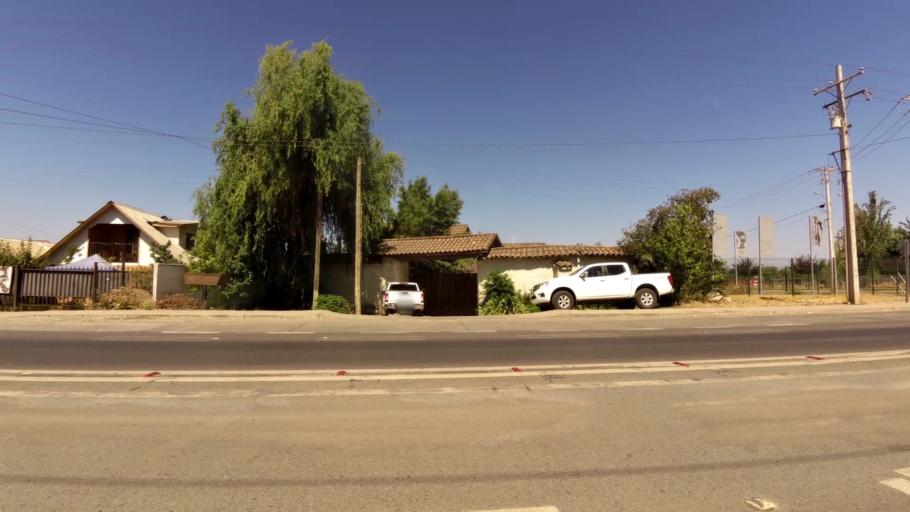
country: CL
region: Maule
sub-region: Provincia de Talca
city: Talca
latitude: -35.4311
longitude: -71.6071
